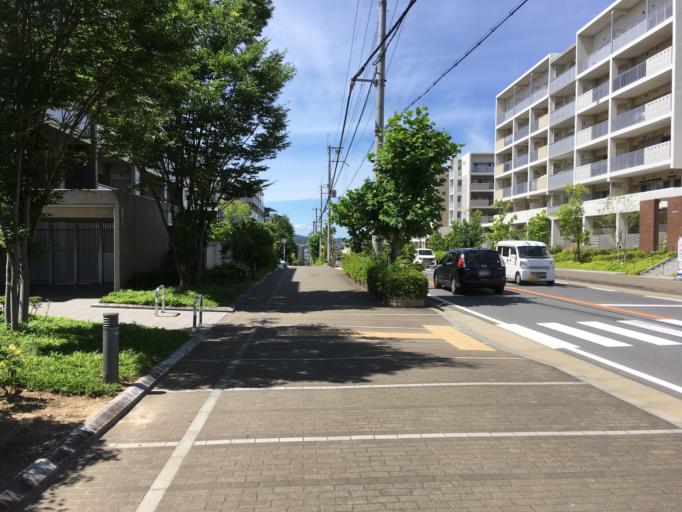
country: JP
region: Nara
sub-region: Ikoma-shi
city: Ikoma
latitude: 34.7008
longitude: 135.7506
